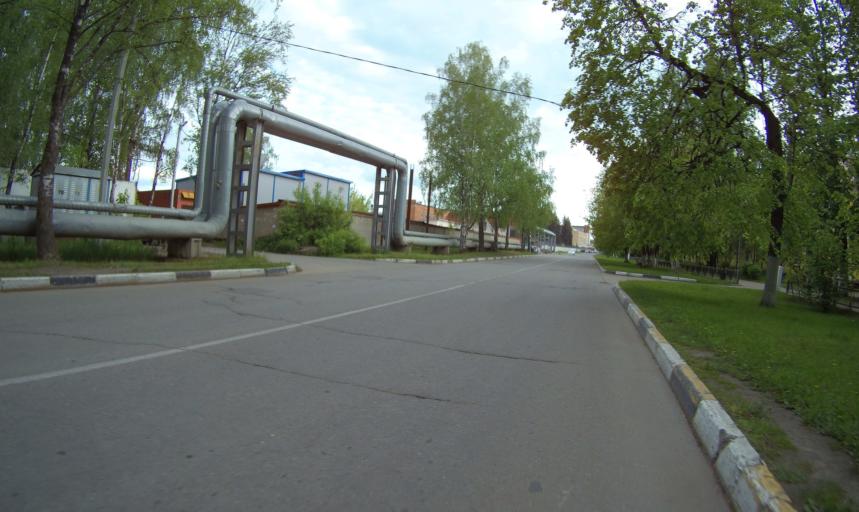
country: RU
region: Moskovskaya
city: Ramenskoye
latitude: 55.5693
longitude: 38.2455
